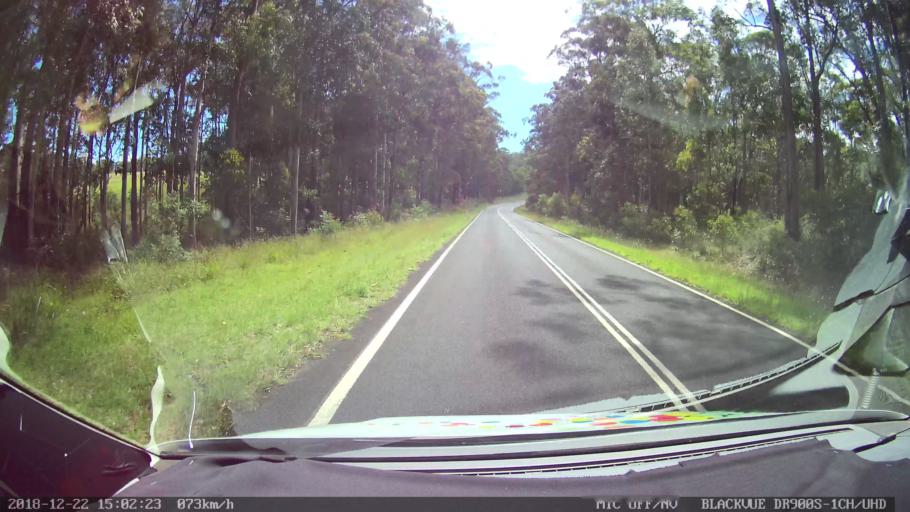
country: AU
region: New South Wales
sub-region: Bellingen
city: Dorrigo
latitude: -30.2610
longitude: 152.4517
